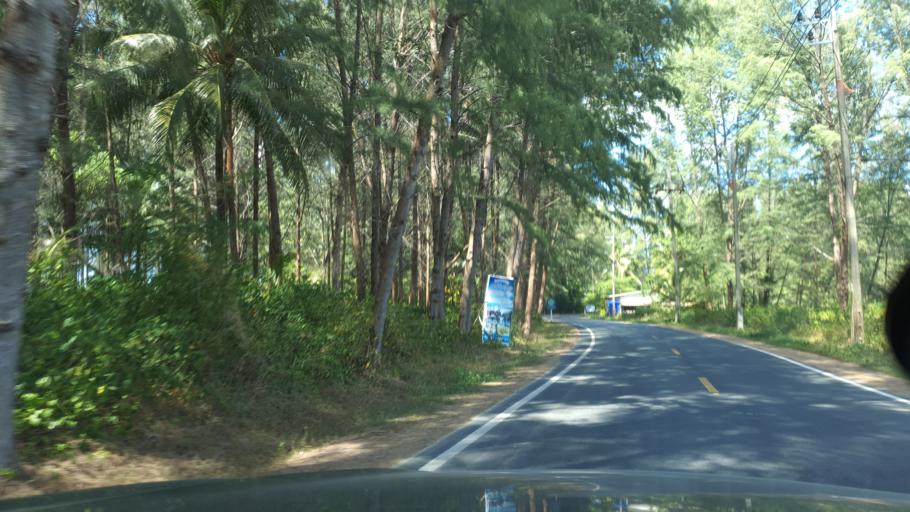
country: TH
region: Phangnga
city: Thai Mueang
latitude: 8.2898
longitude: 98.2743
